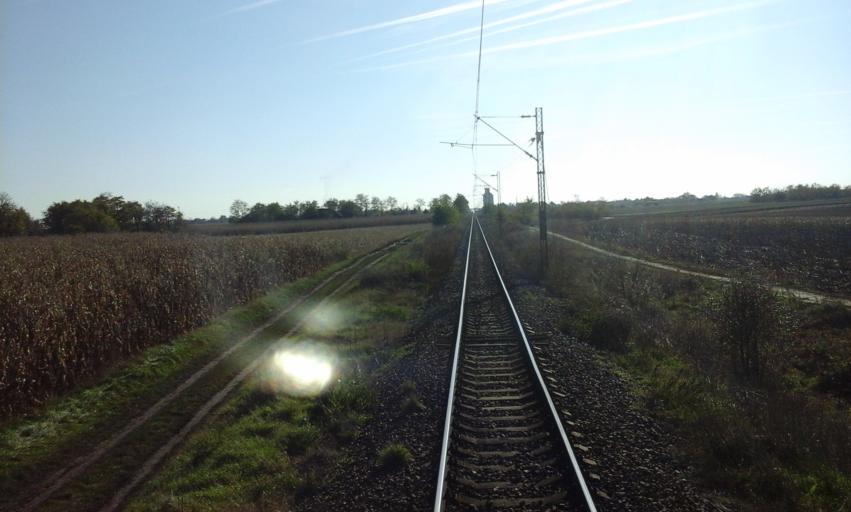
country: RS
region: Autonomna Pokrajina Vojvodina
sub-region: Severnobacki Okrug
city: Subotica
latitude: 45.9575
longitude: 19.6710
